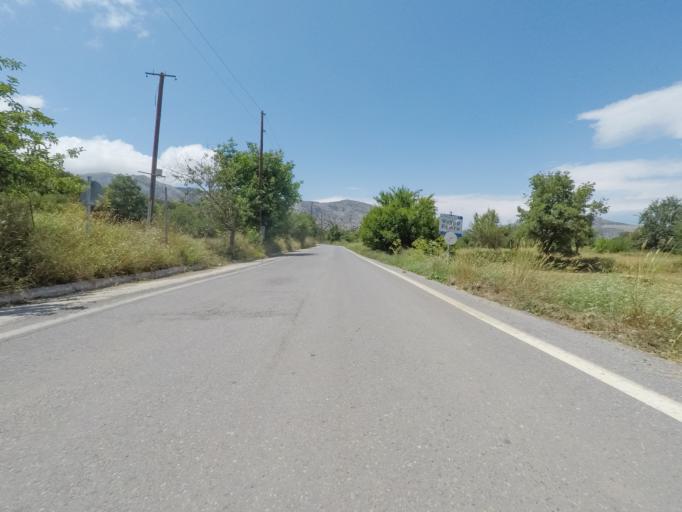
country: GR
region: Crete
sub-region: Nomos Irakleiou
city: Mokhos
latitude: 35.1674
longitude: 25.4488
